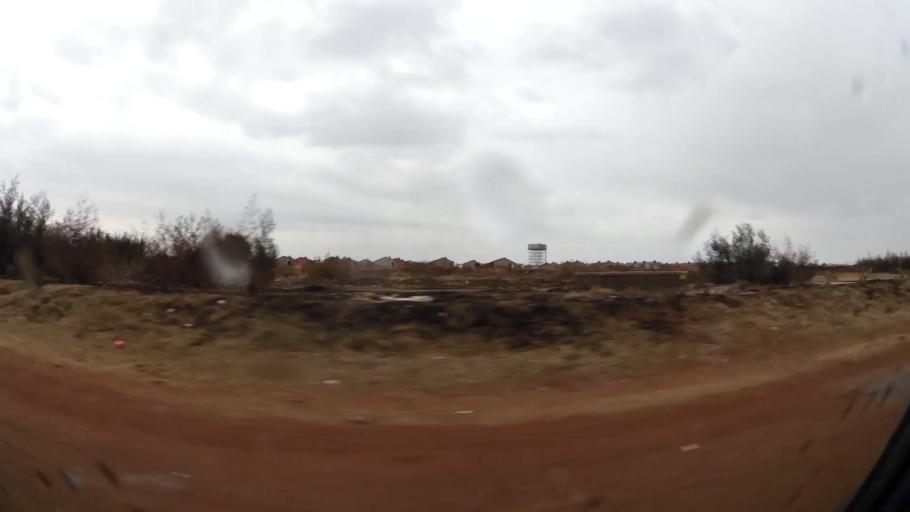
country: ZA
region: Gauteng
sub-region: City of Johannesburg Metropolitan Municipality
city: Roodepoort
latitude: -26.1729
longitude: 27.7995
